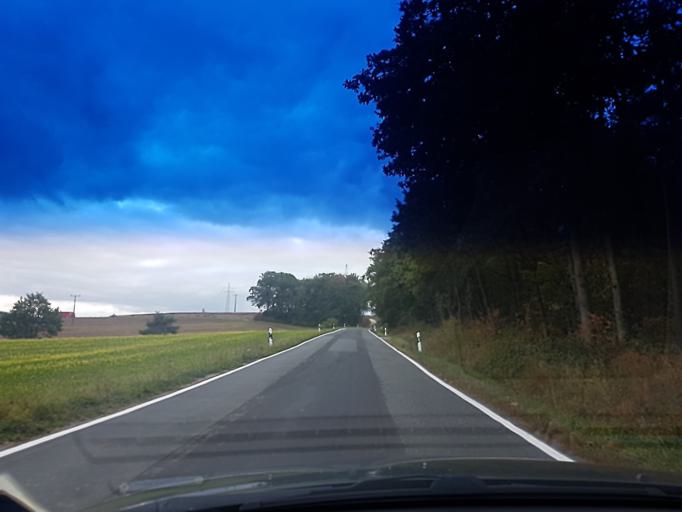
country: DE
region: Bavaria
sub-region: Regierungsbezirk Mittelfranken
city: Hochstadt an der Aisch
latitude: 49.7249
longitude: 10.8315
